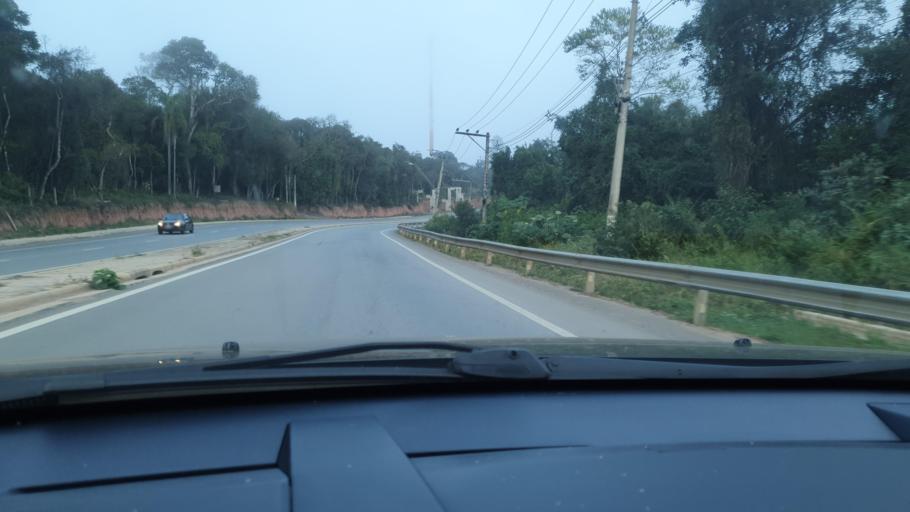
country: BR
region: Sao Paulo
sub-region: Ibiuna
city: Ibiuna
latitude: -23.6545
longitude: -47.1833
